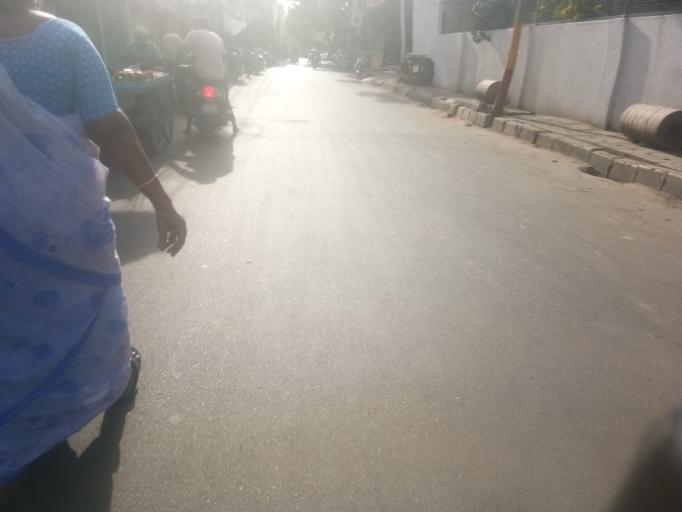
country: IN
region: Karnataka
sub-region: Bangalore Urban
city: Bangalore
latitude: 13.0031
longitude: 77.6035
